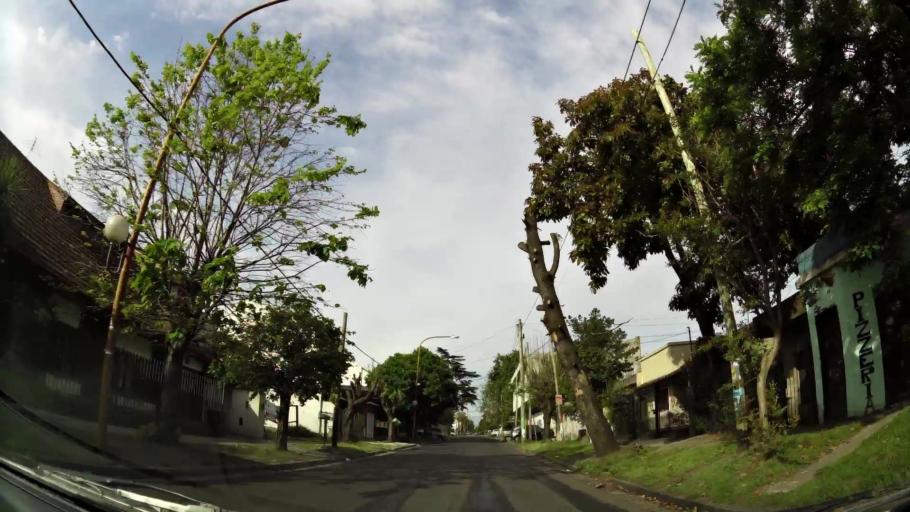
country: AR
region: Buenos Aires
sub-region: Partido de Quilmes
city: Quilmes
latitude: -34.7560
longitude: -58.2865
